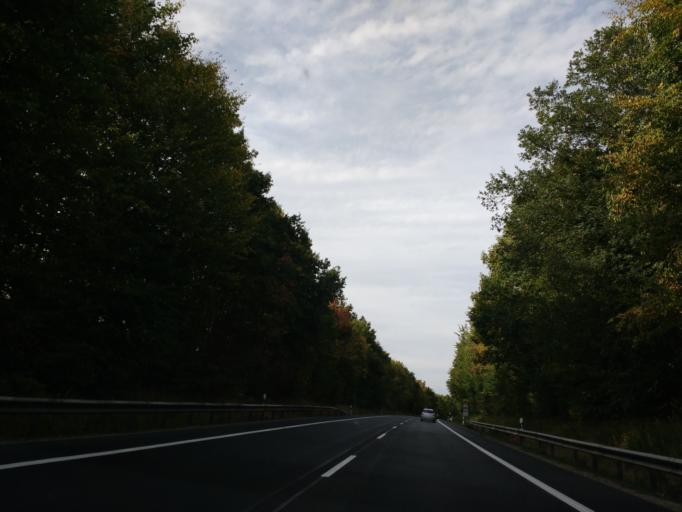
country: DE
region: North Rhine-Westphalia
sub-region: Regierungsbezirk Detmold
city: Blomberg
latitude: 51.9106
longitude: 9.0847
